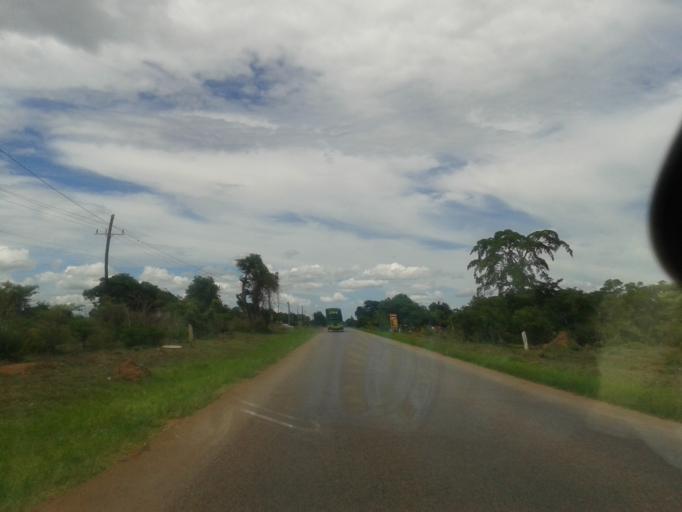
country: UG
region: Western Region
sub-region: Kiryandongo District
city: Masindi Port
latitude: 1.5184
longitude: 32.0576
